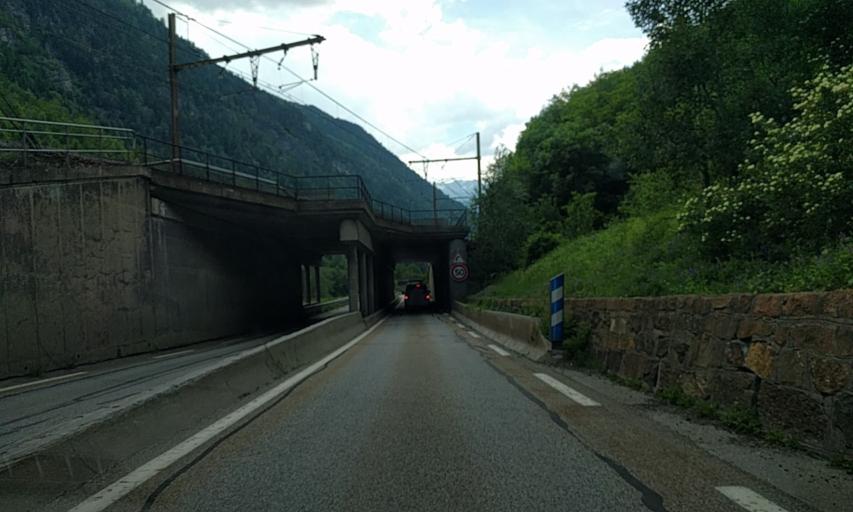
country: FR
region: Rhone-Alpes
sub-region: Departement de la Savoie
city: Saint-Michel-de-Maurienne
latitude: 45.2077
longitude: 6.5349
